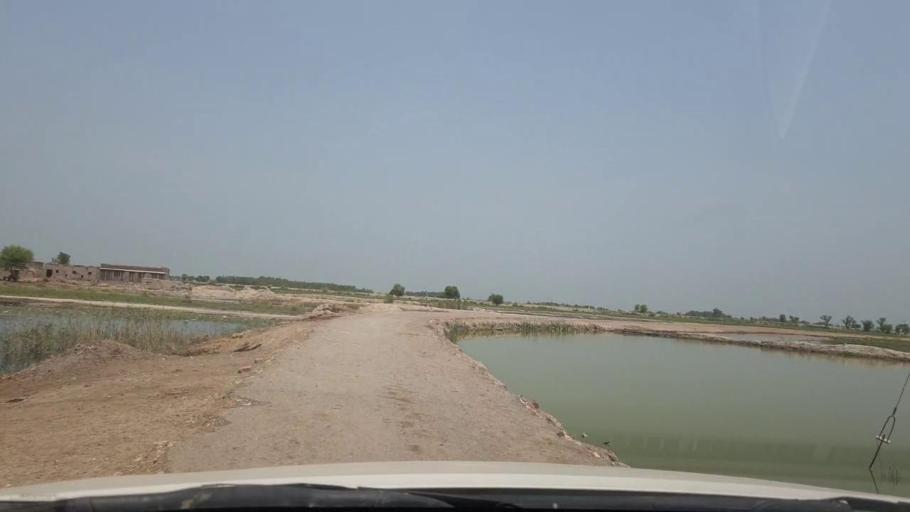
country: PK
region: Sindh
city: Rustam jo Goth
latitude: 28.0180
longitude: 68.7835
